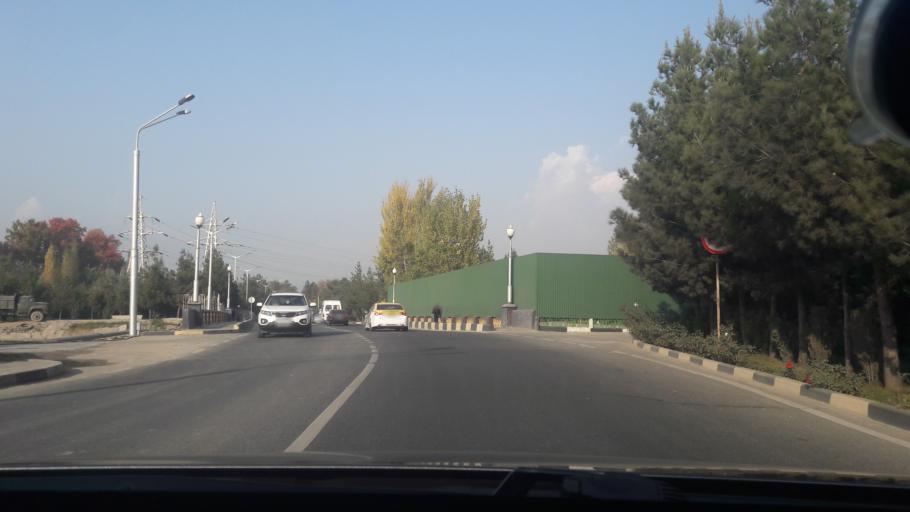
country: TJ
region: Dushanbe
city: Dushanbe
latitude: 38.5798
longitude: 68.7732
